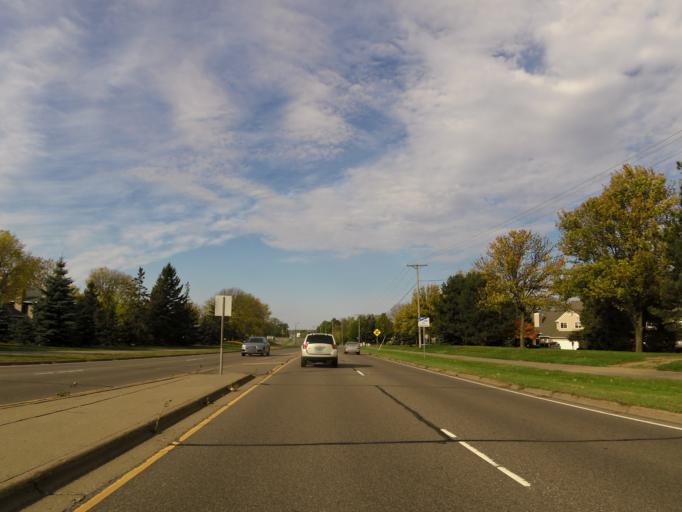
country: US
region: Minnesota
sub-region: Dakota County
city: Eagan
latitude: 44.8045
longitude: -93.1985
